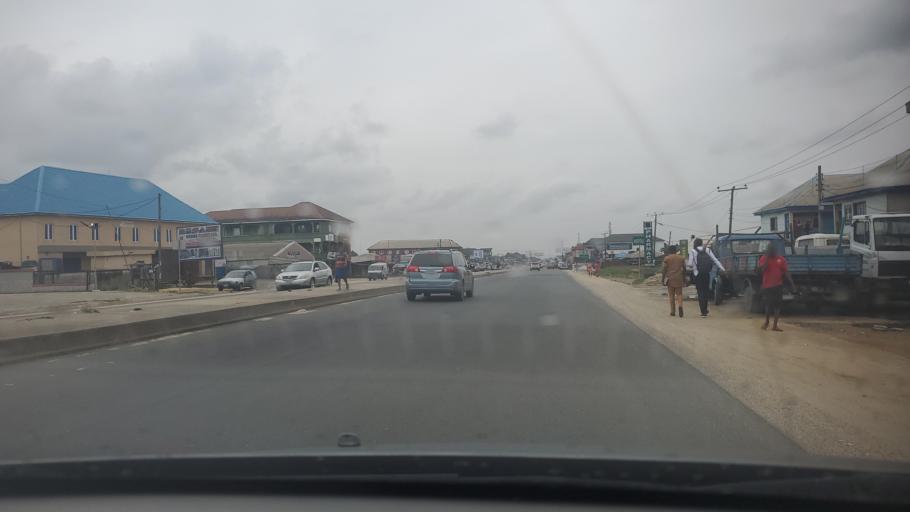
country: NG
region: Rivers
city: Port Harcourt
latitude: 4.8694
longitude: 6.9788
